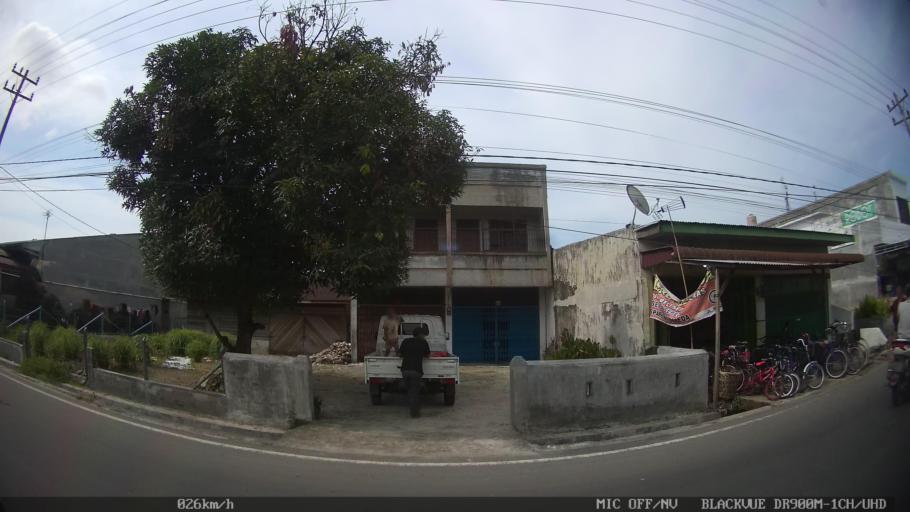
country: ID
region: North Sumatra
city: Percut
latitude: 3.6072
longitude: 98.7685
